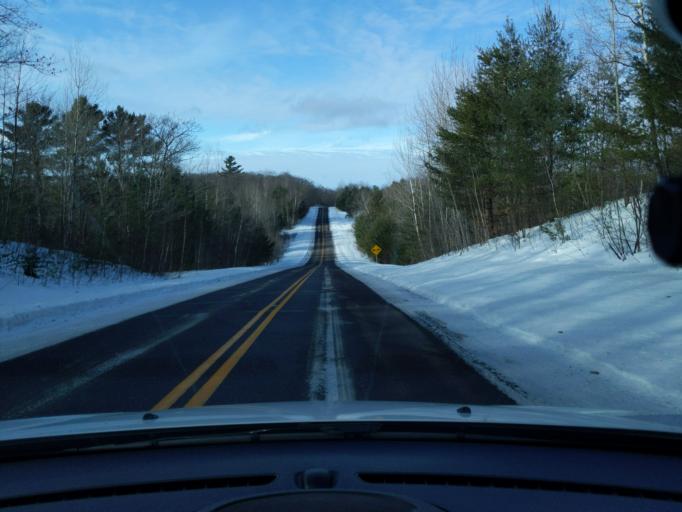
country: US
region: Wisconsin
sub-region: Sawyer County
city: Little Round Lake
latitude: 46.1155
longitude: -91.3319
